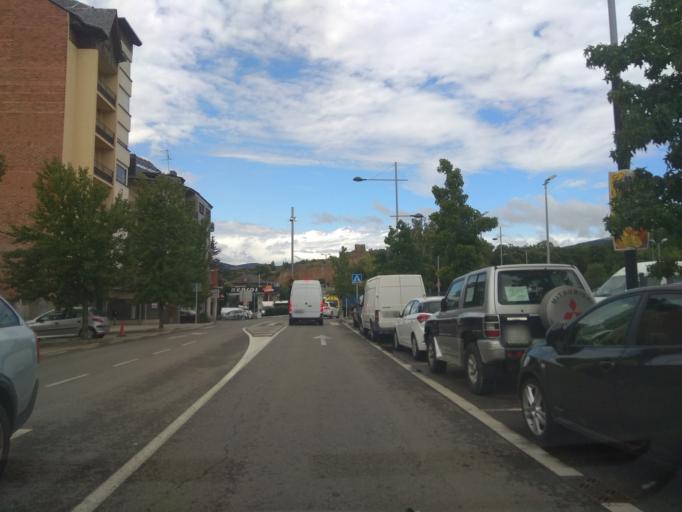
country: ES
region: Catalonia
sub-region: Provincia de Lleida
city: la Seu d'Urgell
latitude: 42.3604
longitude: 1.4562
